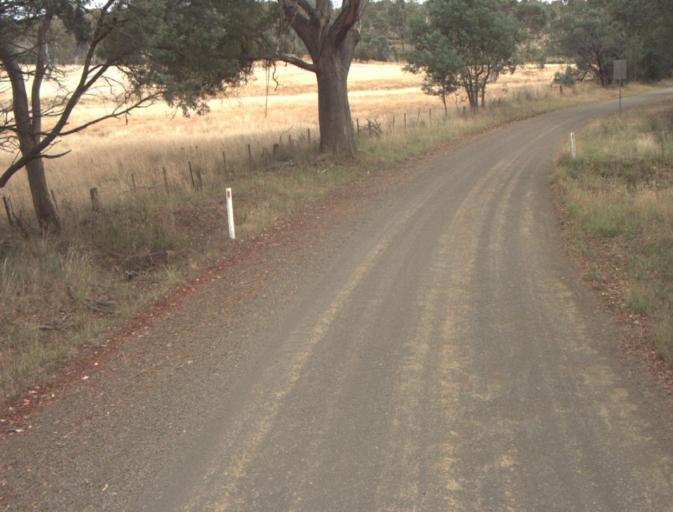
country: AU
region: Tasmania
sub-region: Northern Midlands
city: Evandale
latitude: -41.5299
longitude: 147.3561
